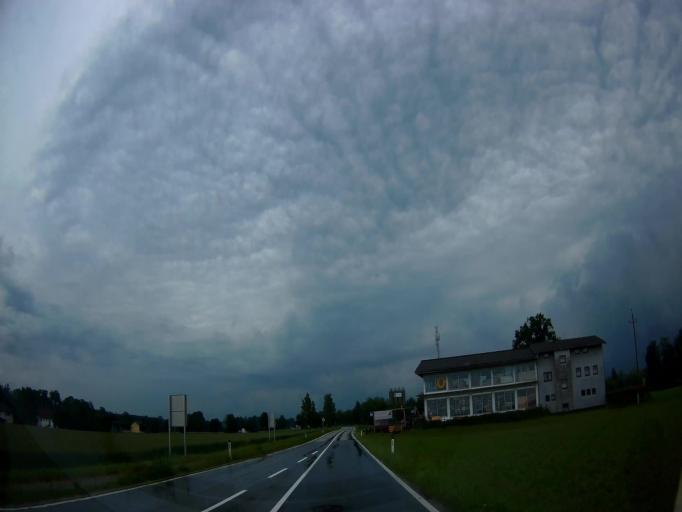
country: AT
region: Salzburg
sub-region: Politischer Bezirk Salzburg-Umgebung
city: Mattsee
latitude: 48.0668
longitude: 13.1435
